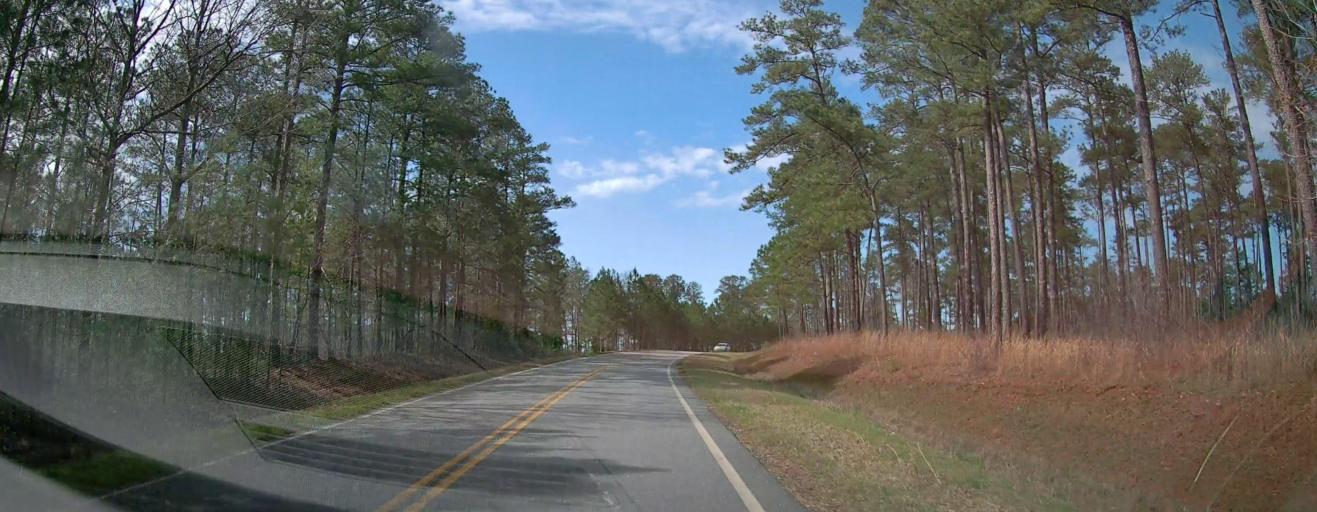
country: US
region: Georgia
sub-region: Monroe County
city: Forsyth
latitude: 33.0780
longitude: -83.7398
